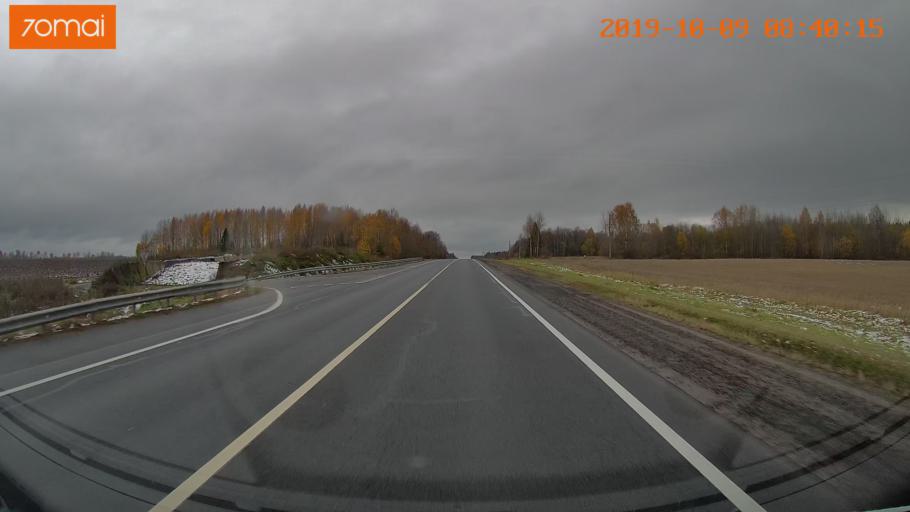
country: RU
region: Vologda
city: Gryazovets
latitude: 58.9837
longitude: 40.1428
